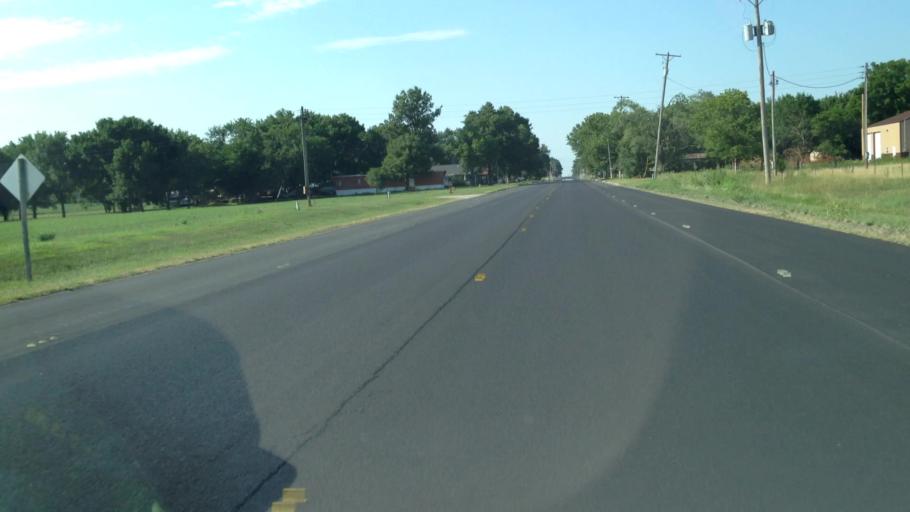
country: US
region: Kansas
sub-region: Allen County
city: Iola
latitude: 37.9089
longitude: -95.1702
